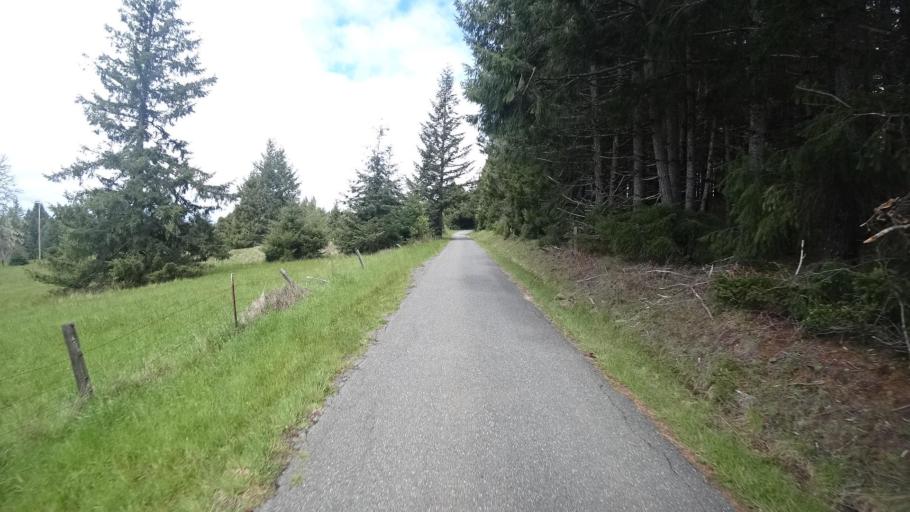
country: US
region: California
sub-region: Humboldt County
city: Blue Lake
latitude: 40.7921
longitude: -123.9704
